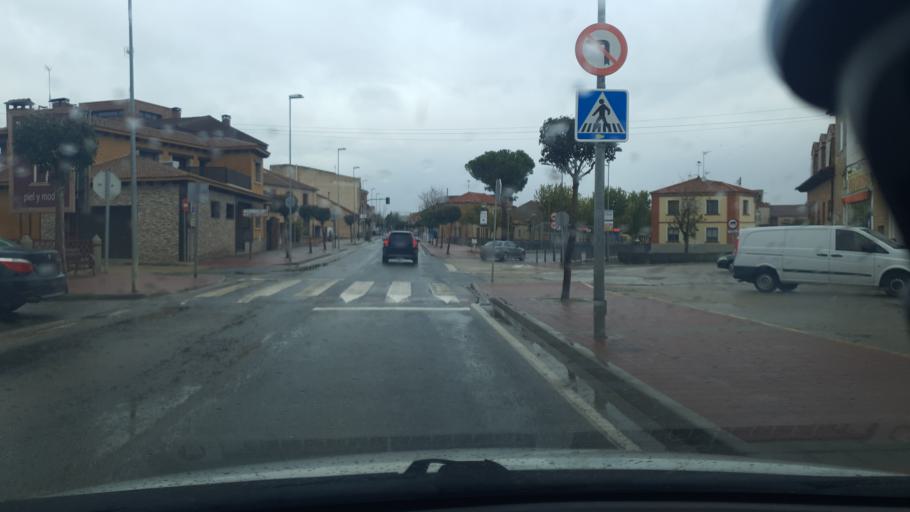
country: ES
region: Castille and Leon
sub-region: Provincia de Segovia
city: Carbonero el Mayor
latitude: 41.1183
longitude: -4.2641
